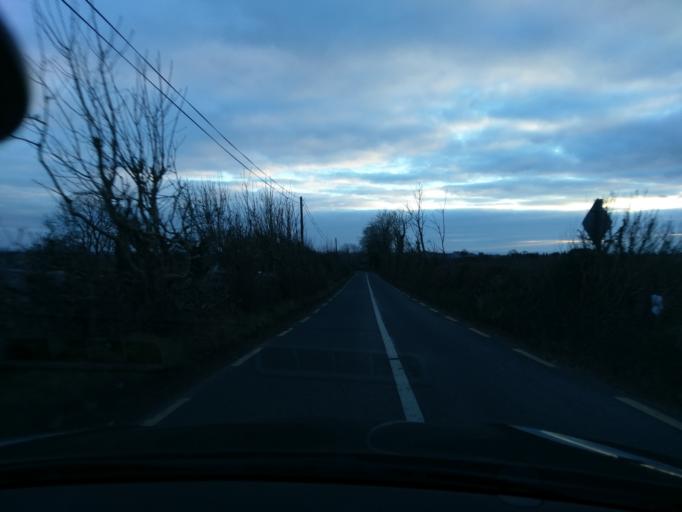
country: IE
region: Connaught
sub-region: County Galway
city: Athenry
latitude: 53.3650
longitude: -8.7738
